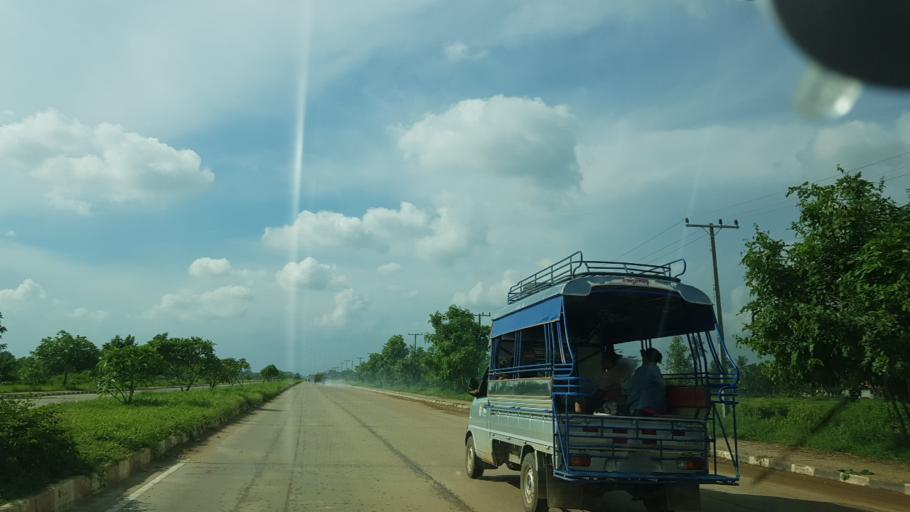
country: TH
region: Nong Khai
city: Nong Khai
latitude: 17.8889
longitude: 102.7209
